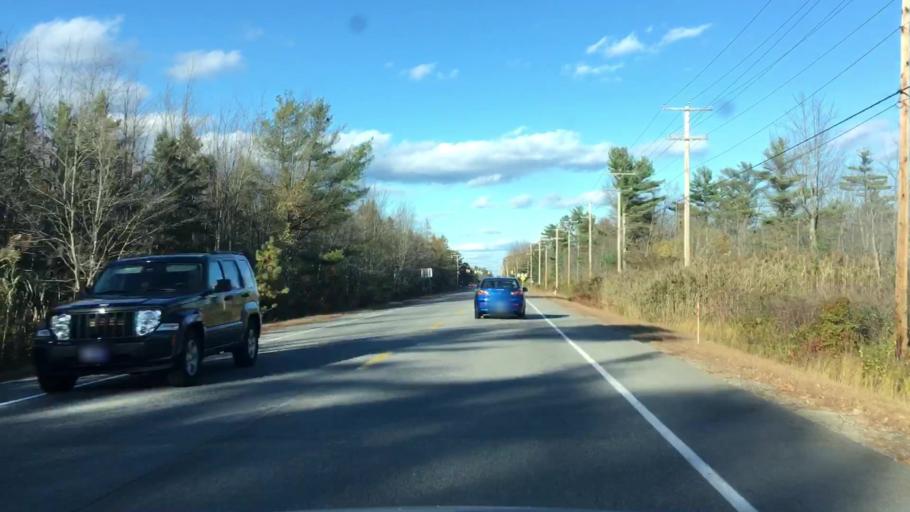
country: US
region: Maine
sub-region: Cumberland County
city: West Scarborough
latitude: 43.6058
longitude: -70.3640
